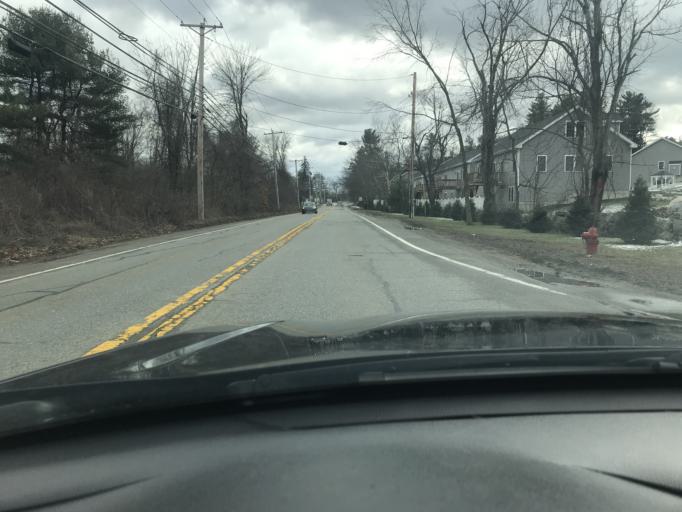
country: US
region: Massachusetts
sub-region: Middlesex County
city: Tyngsboro
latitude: 42.6606
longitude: -71.4065
